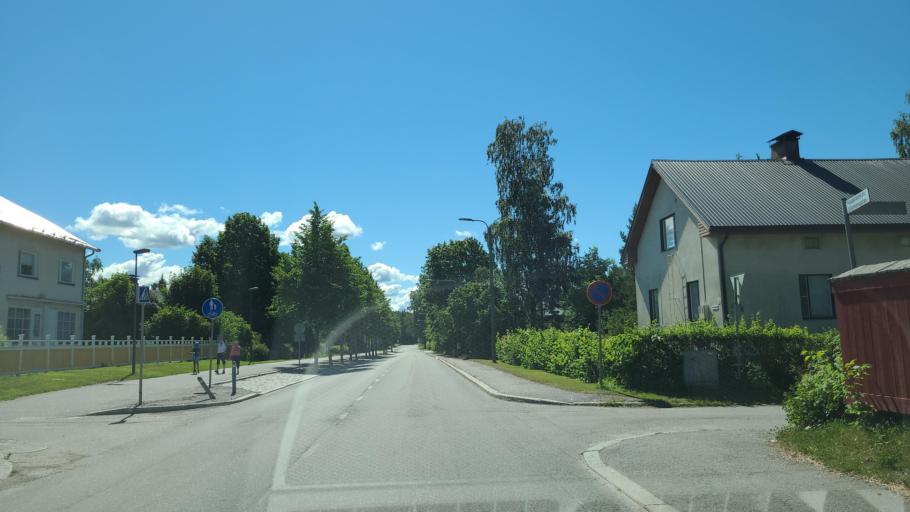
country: FI
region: Ostrobothnia
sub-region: Vaasa
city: Ristinummi
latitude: 63.0721
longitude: 21.7227
